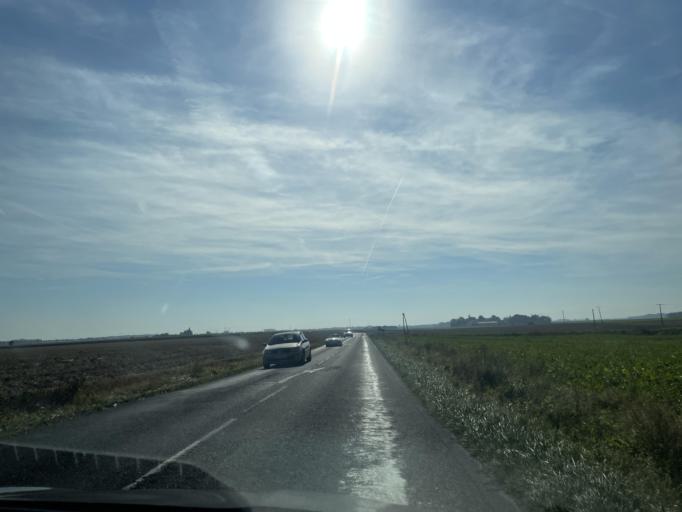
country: FR
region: Ile-de-France
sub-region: Departement de Seine-et-Marne
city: Sammeron
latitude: 48.8860
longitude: 3.0683
